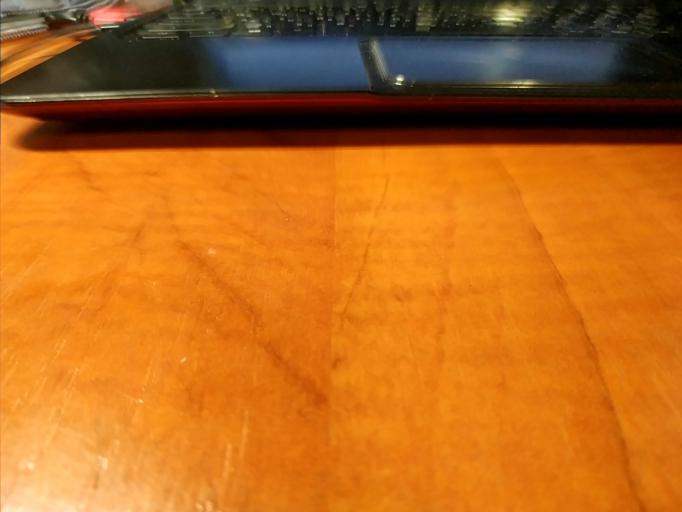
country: RU
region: Tverskaya
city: Ves'yegonsk
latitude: 58.7904
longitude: 37.5441
